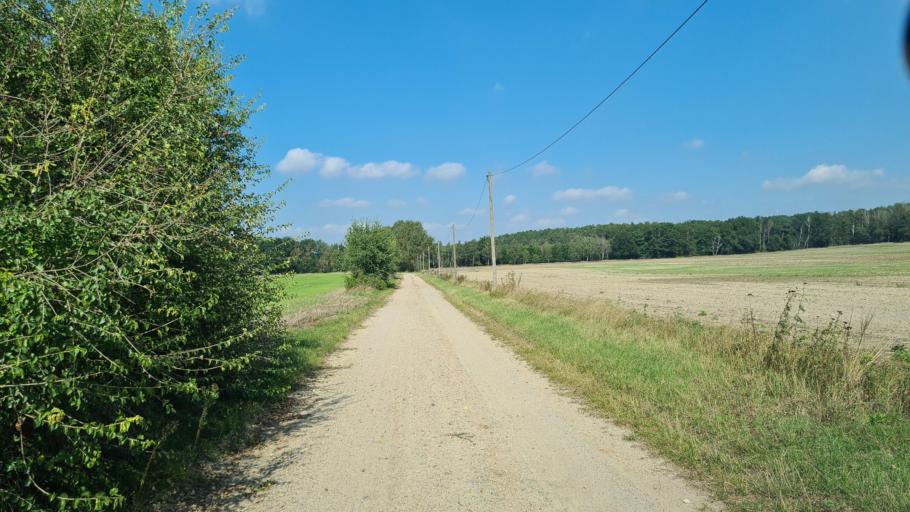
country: DE
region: Brandenburg
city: Sonnewalde
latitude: 51.7242
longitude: 13.6503
